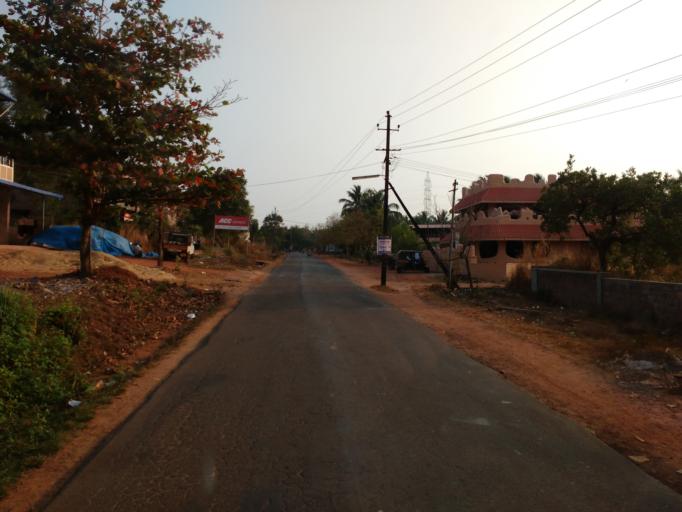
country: IN
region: Karnataka
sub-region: Dakshina Kannada
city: Mangalore
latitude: 12.9216
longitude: 74.8980
